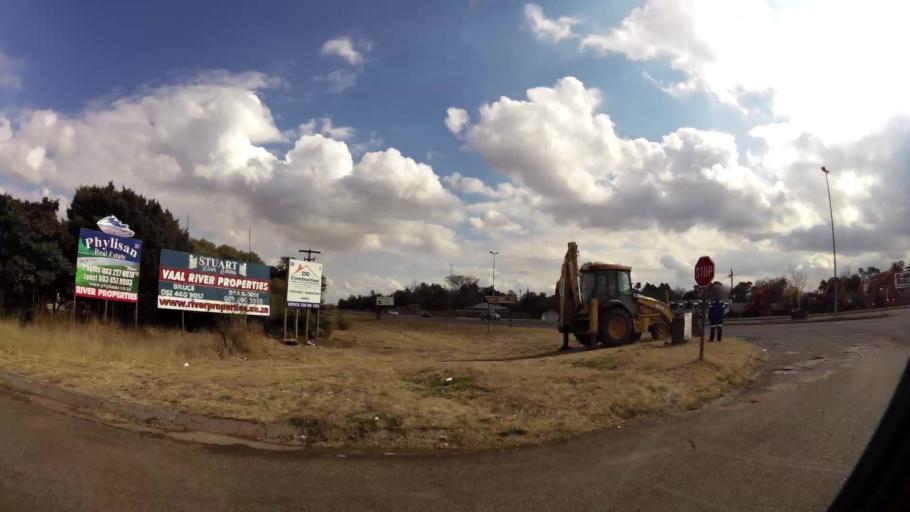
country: ZA
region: Gauteng
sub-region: Sedibeng District Municipality
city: Vanderbijlpark
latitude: -26.7393
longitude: 27.8197
